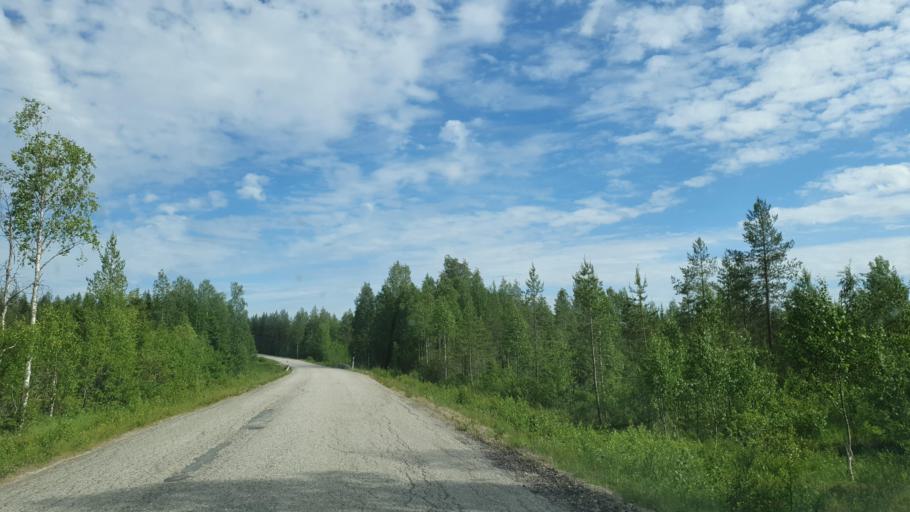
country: FI
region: Kainuu
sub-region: Kehys-Kainuu
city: Kuhmo
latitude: 64.5314
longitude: 29.3450
